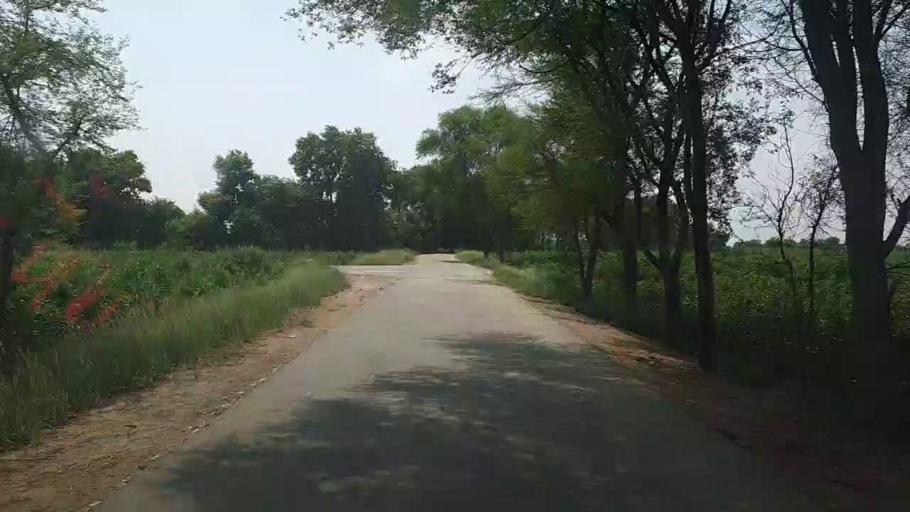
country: PK
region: Sindh
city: Ubauro
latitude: 28.1741
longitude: 69.8252
